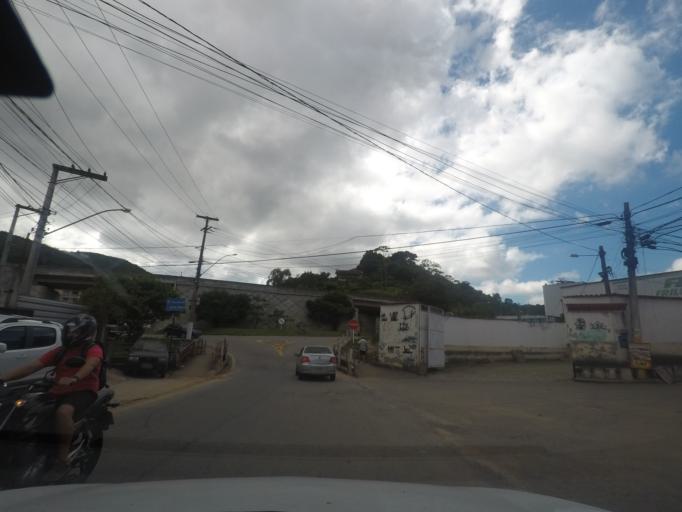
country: BR
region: Rio de Janeiro
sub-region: Teresopolis
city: Teresopolis
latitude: -22.3889
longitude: -42.9539
